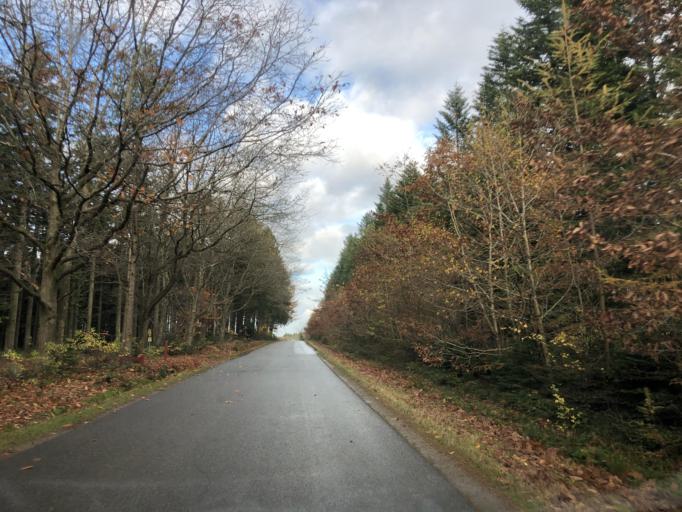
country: DK
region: Central Jutland
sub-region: Holstebro Kommune
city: Ulfborg
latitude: 56.1774
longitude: 8.4199
